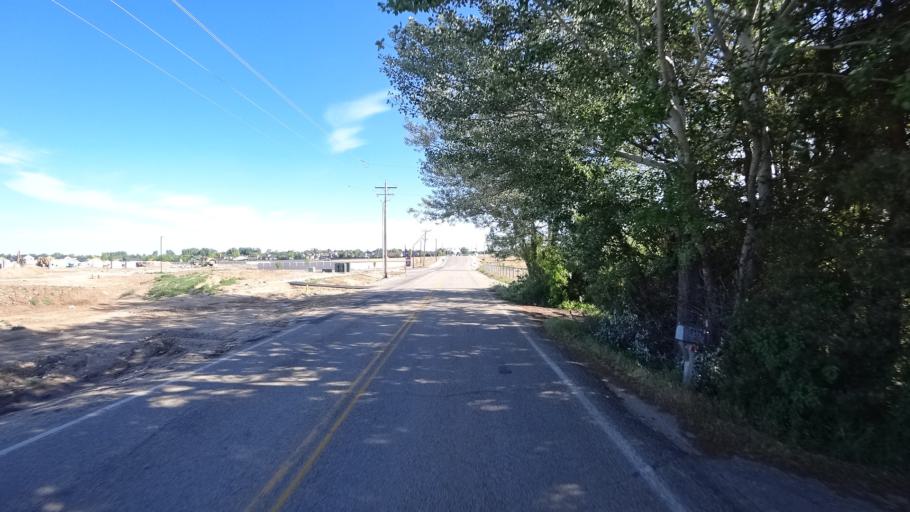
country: US
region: Idaho
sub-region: Ada County
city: Garden City
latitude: 43.5389
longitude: -116.2744
